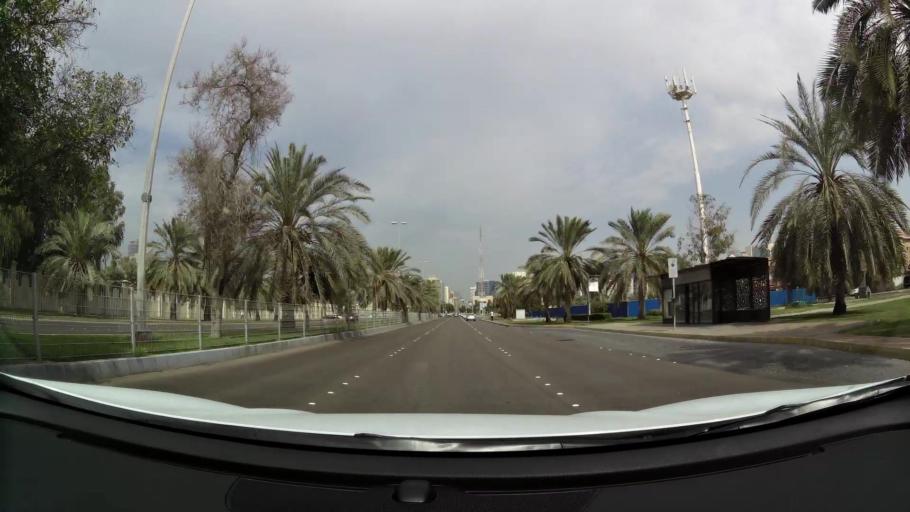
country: AE
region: Abu Dhabi
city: Abu Dhabi
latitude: 24.4706
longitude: 54.3591
